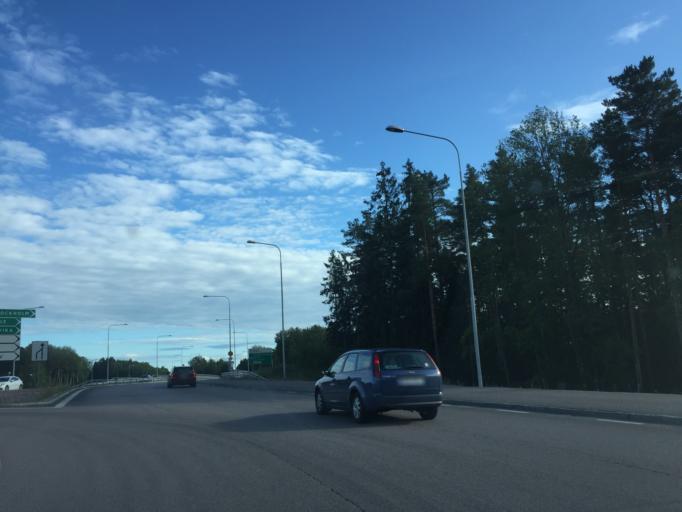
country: SE
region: Vaestmanland
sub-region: Vasteras
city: Vasteras
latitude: 59.6063
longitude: 16.4506
